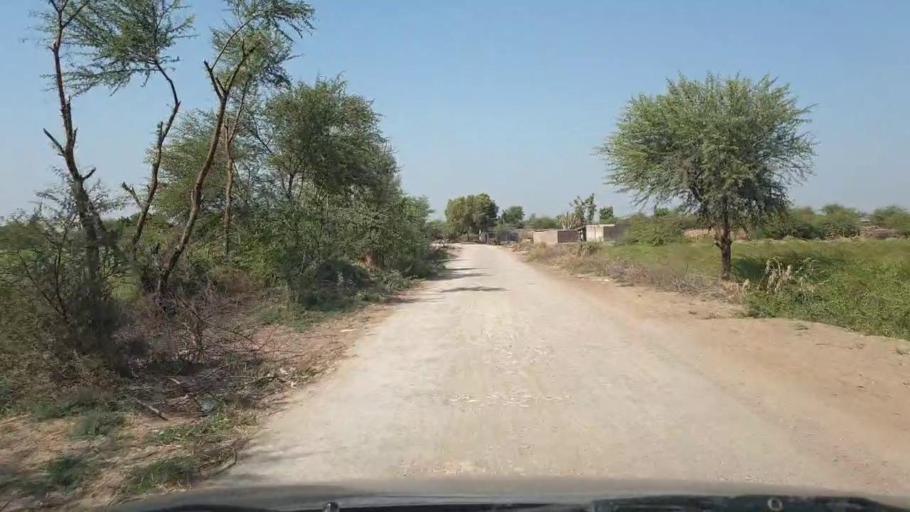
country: PK
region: Sindh
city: Samaro
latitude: 25.2364
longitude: 69.2703
